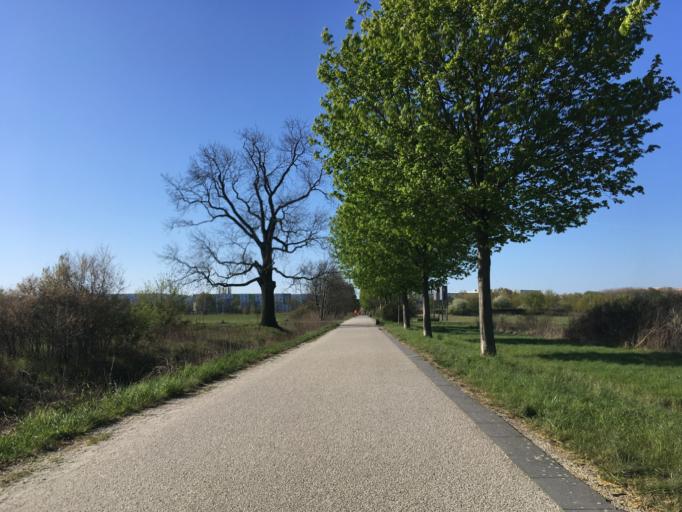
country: DE
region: Berlin
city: Wartenberg
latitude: 52.5816
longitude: 13.5037
